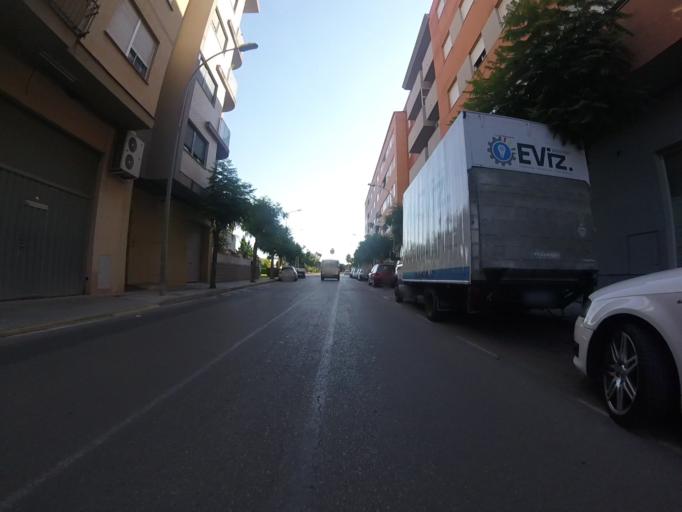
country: ES
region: Valencia
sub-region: Provincia de Castello
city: Benicarlo
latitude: 40.4226
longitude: 0.4290
